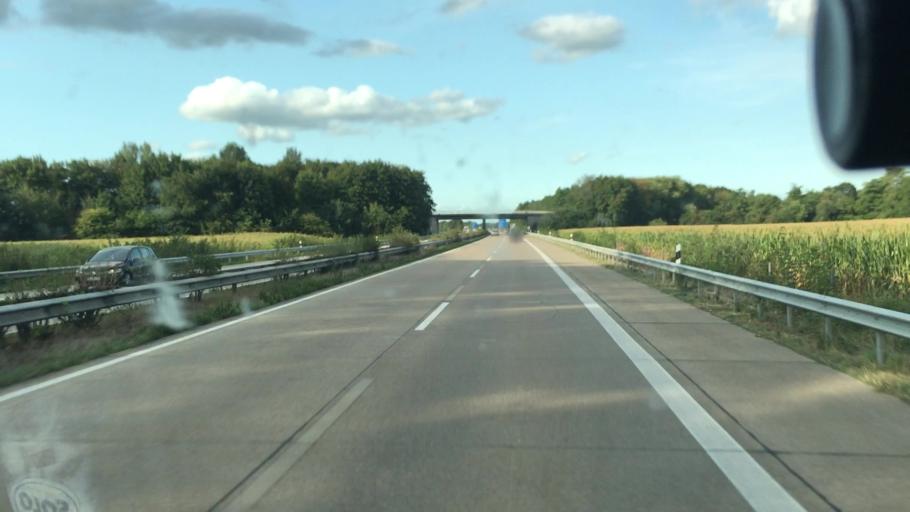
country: DE
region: Lower Saxony
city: Wardenburg
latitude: 53.0919
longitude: 8.2624
